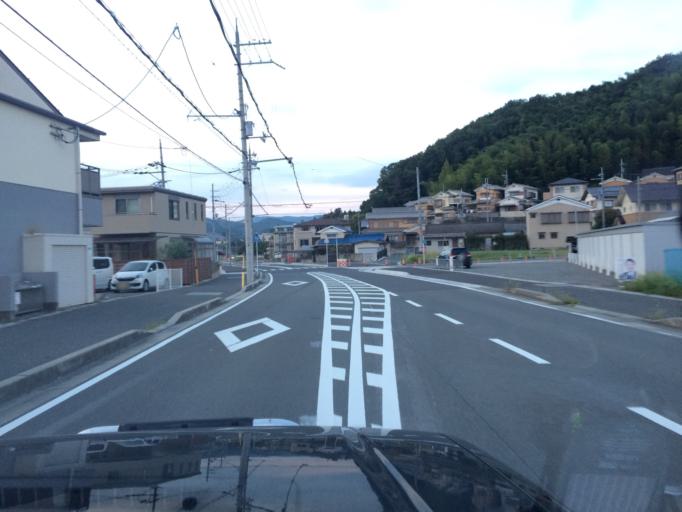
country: JP
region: Kyoto
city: Kameoka
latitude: 35.1006
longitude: 135.4745
